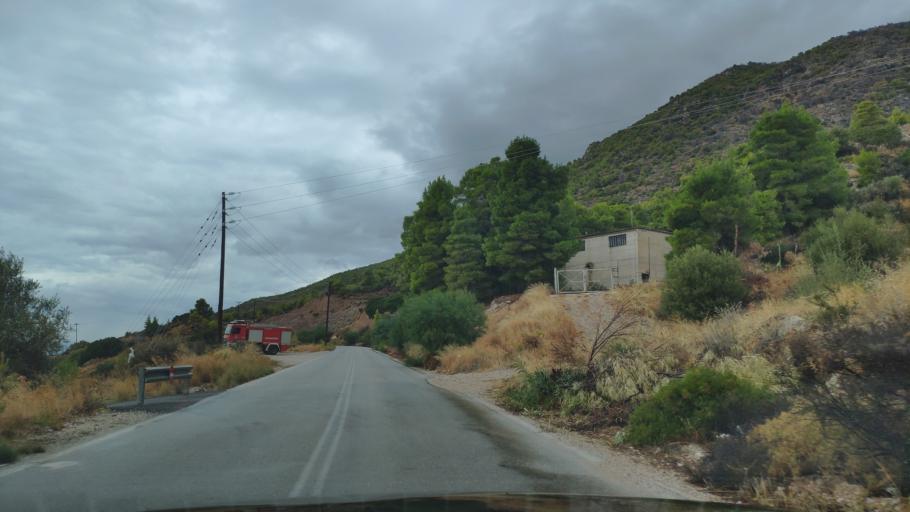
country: GR
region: Peloponnese
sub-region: Nomos Korinthias
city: Loutraki
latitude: 37.9790
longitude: 22.9866
